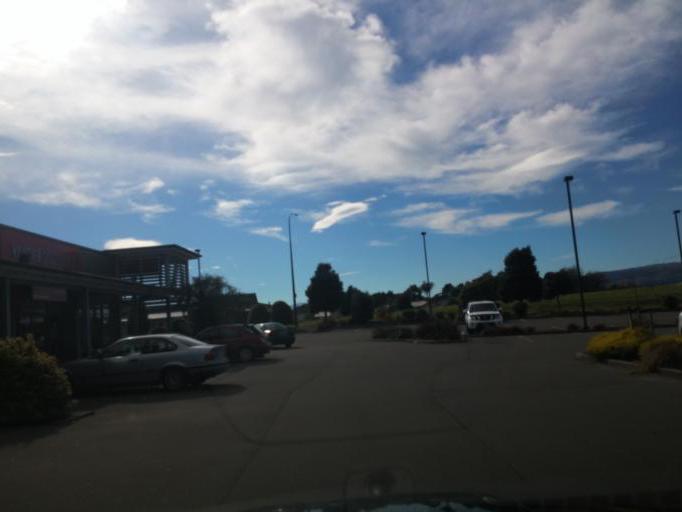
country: NZ
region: Manawatu-Wanganui
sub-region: Palmerston North City
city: Palmerston North
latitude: -40.3874
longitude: 175.6388
